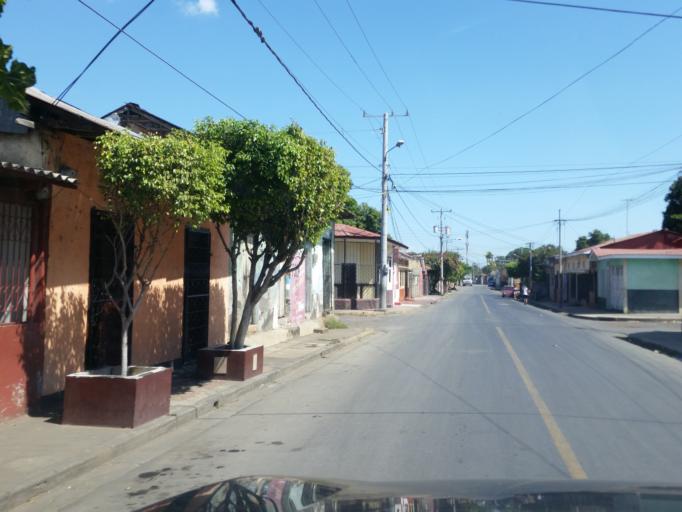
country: NI
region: Managua
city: Managua
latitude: 12.1596
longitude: -86.2852
